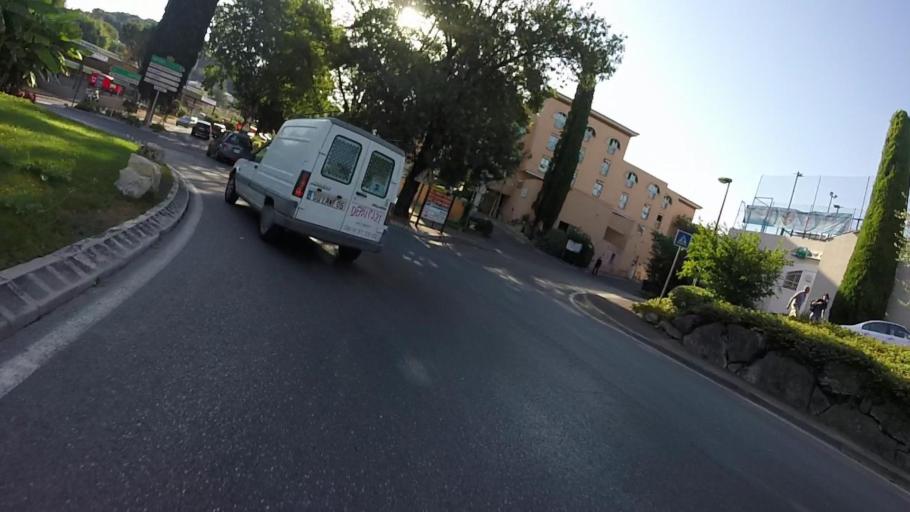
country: FR
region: Provence-Alpes-Cote d'Azur
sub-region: Departement des Alpes-Maritimes
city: Mougins
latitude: 43.6050
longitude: 6.9875
